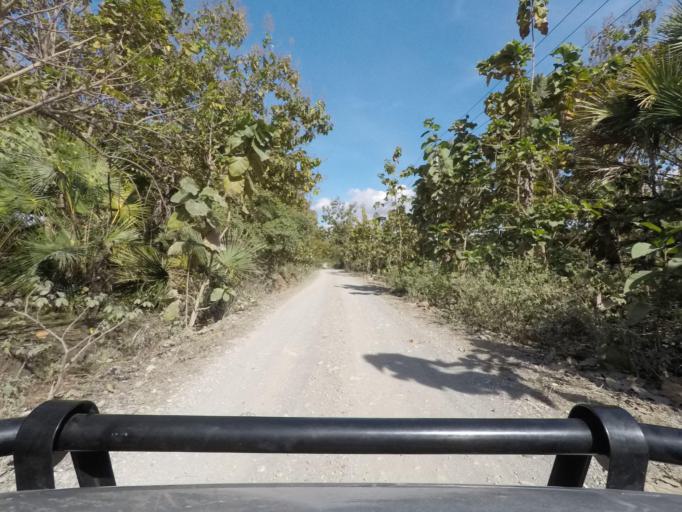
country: ID
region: East Nusa Tenggara
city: Atambua
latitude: -8.9557
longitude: 124.9594
